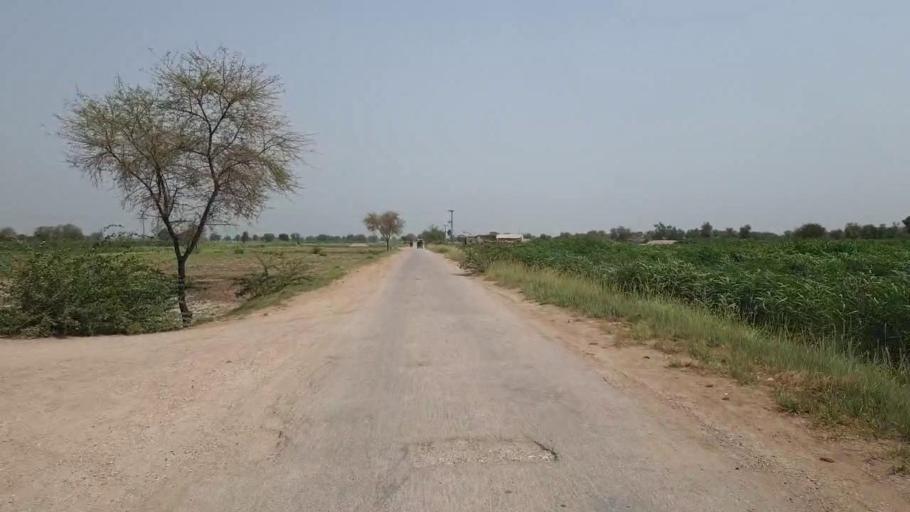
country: PK
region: Sindh
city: Nawabshah
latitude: 26.2577
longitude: 68.3201
